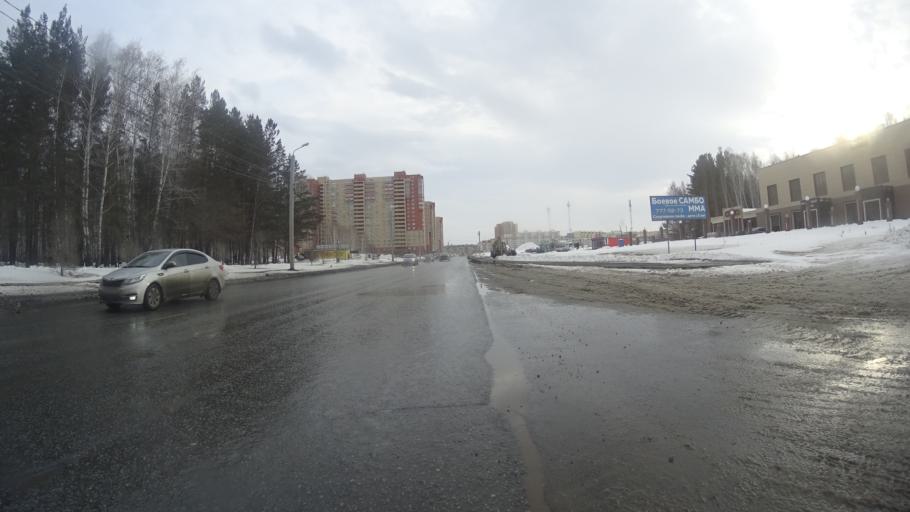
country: RU
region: Chelyabinsk
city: Roshchino
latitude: 55.1983
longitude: 61.2801
